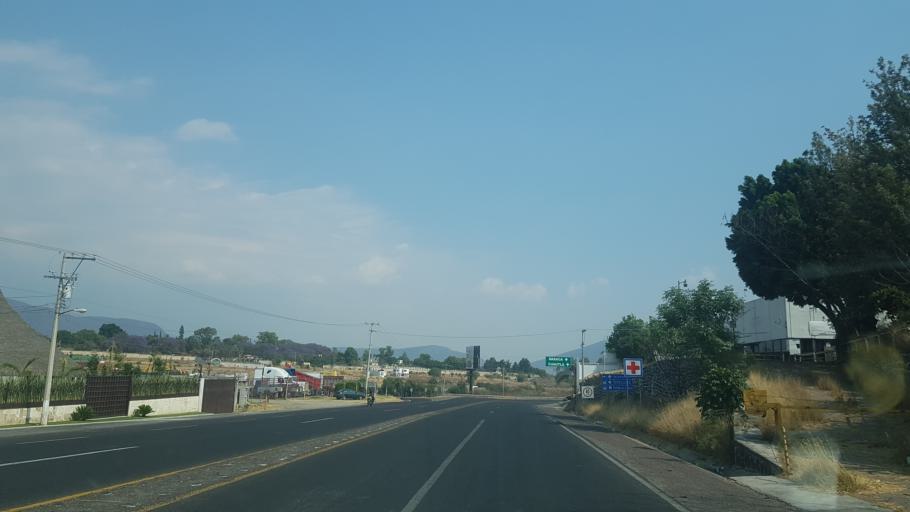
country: MX
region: Puebla
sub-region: Atlixco
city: San Agustin Huixaxtla
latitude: 18.9227
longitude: -98.4100
